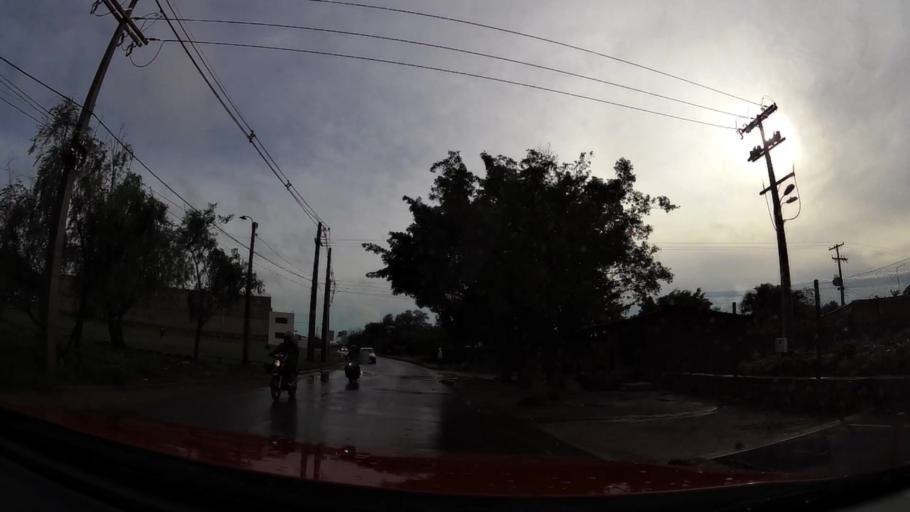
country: PY
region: Central
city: Limpio
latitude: -25.2071
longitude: -57.5059
